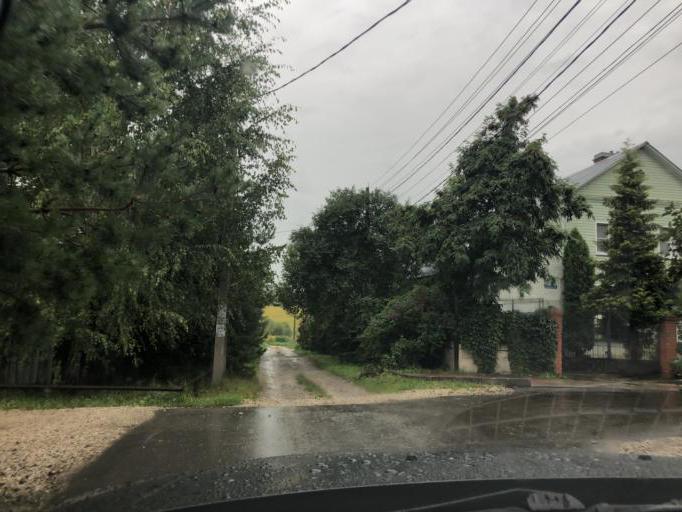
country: RU
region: Tula
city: Barsuki
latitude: 54.2015
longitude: 37.5233
